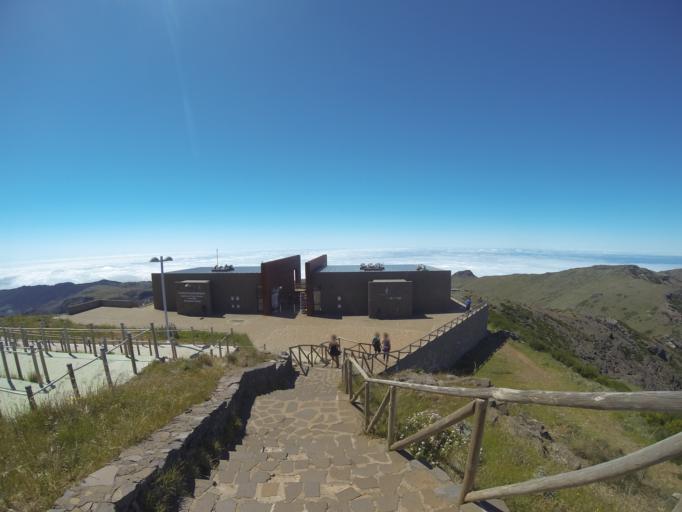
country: PT
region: Madeira
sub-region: Camara de Lobos
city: Curral das Freiras
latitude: 32.7349
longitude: -16.9285
